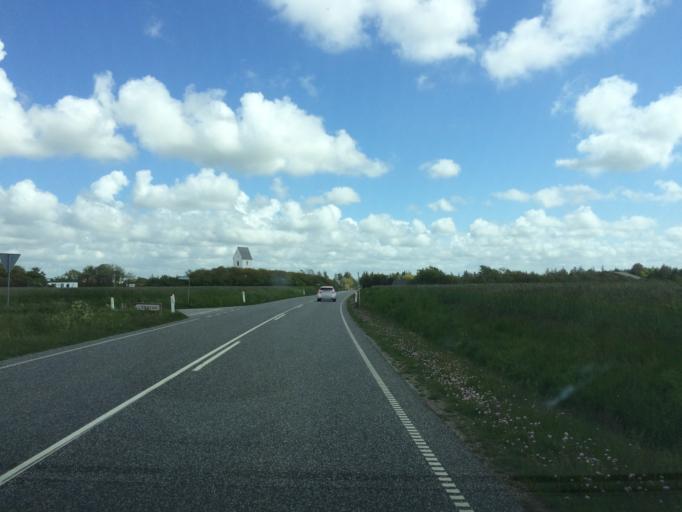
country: DK
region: Central Jutland
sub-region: Holstebro Kommune
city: Ulfborg
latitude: 56.3084
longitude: 8.1807
